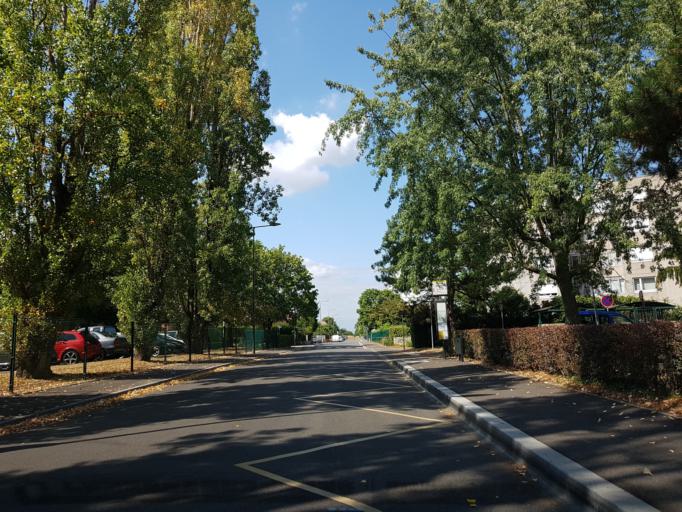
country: FR
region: Alsace
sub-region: Departement du Haut-Rhin
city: Illzach
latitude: 47.7857
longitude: 7.3530
